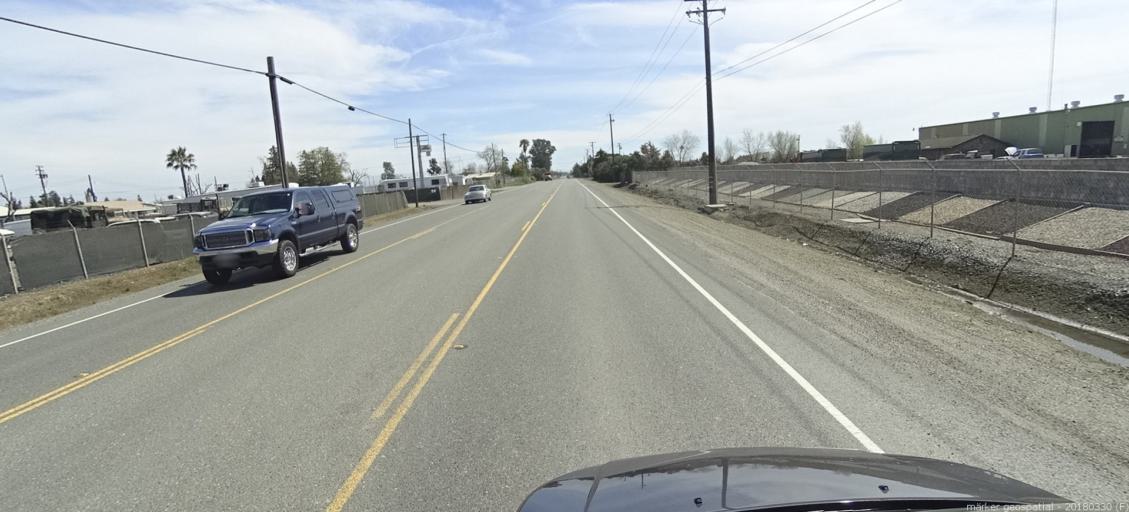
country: US
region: California
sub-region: Sacramento County
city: Rosemont
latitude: 38.5336
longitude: -121.3523
